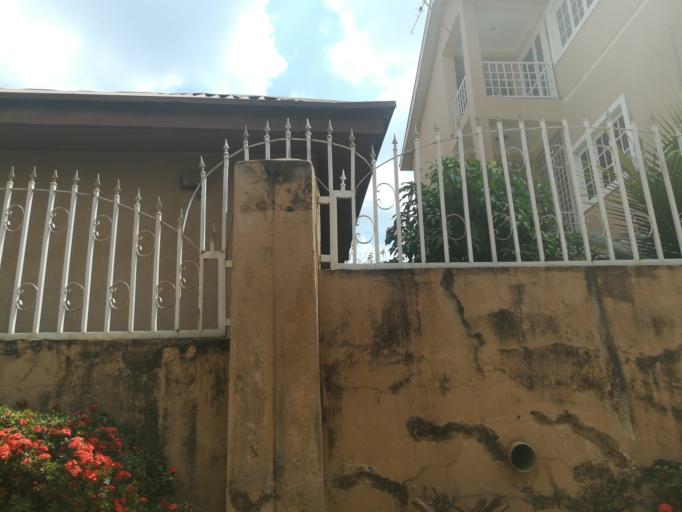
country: NG
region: Abuja Federal Capital Territory
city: Abuja
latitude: 9.0582
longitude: 7.4492
